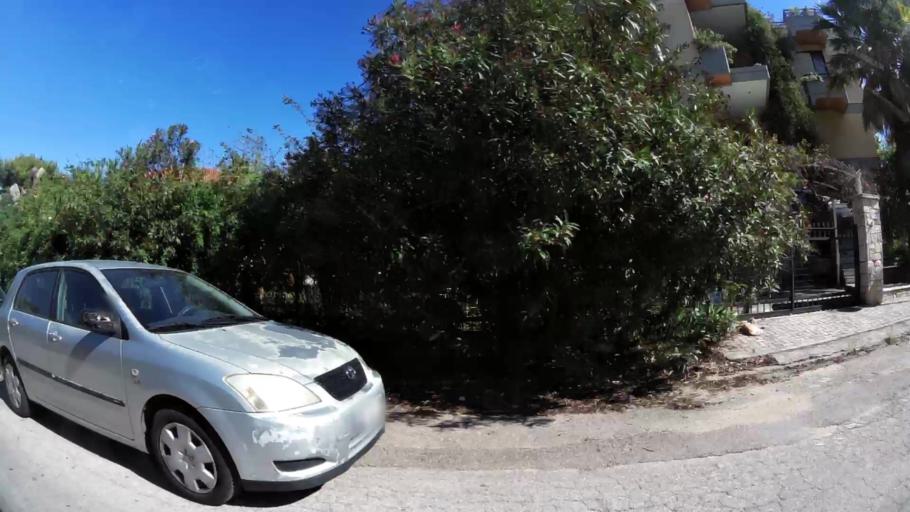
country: GR
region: Attica
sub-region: Nomarchia Athinas
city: Nea Erythraia
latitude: 38.0969
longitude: 23.8093
